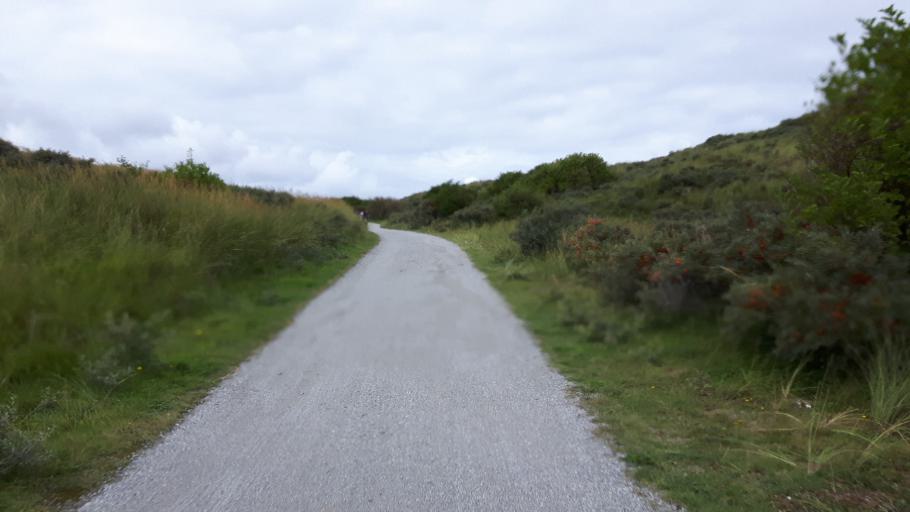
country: NL
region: Friesland
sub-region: Gemeente Ameland
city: Nes
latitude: 53.4578
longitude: 5.7222
